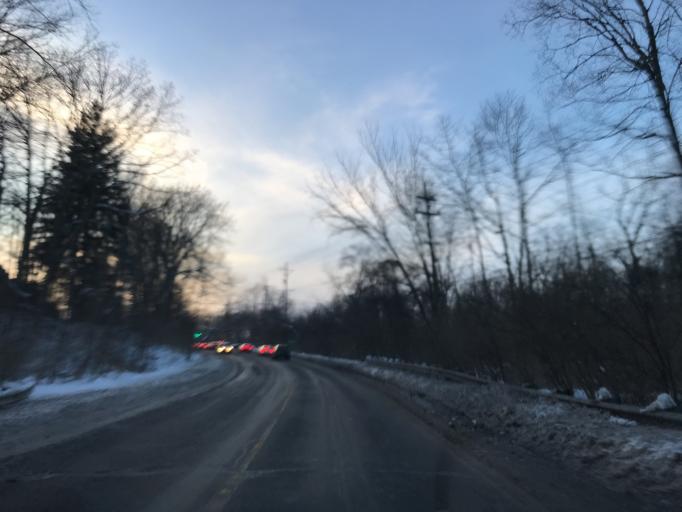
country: US
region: Michigan
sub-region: Oakland County
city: Farmington
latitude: 42.4564
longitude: -83.3149
